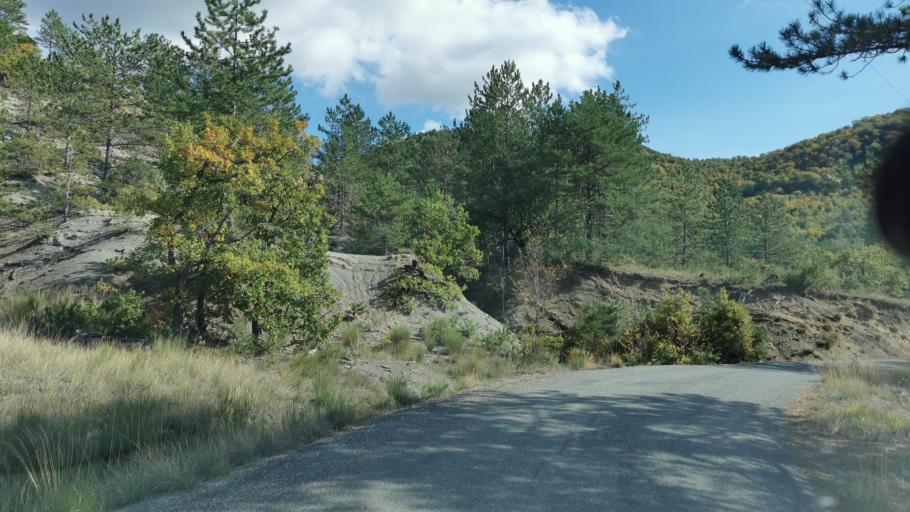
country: FR
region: Provence-Alpes-Cote d'Azur
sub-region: Departement des Alpes-de-Haute-Provence
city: Volonne
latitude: 44.1835
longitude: 6.0261
